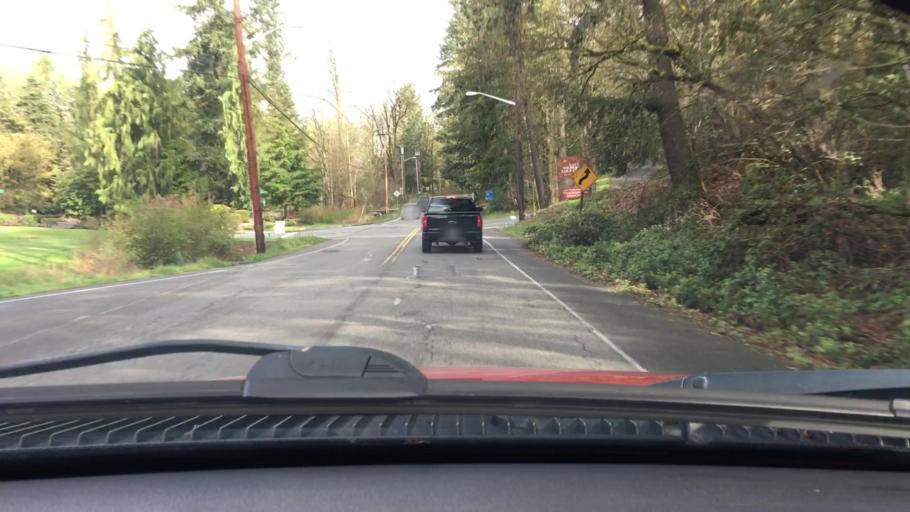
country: US
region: Washington
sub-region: King County
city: Maple Valley
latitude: 47.3733
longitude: -122.0481
